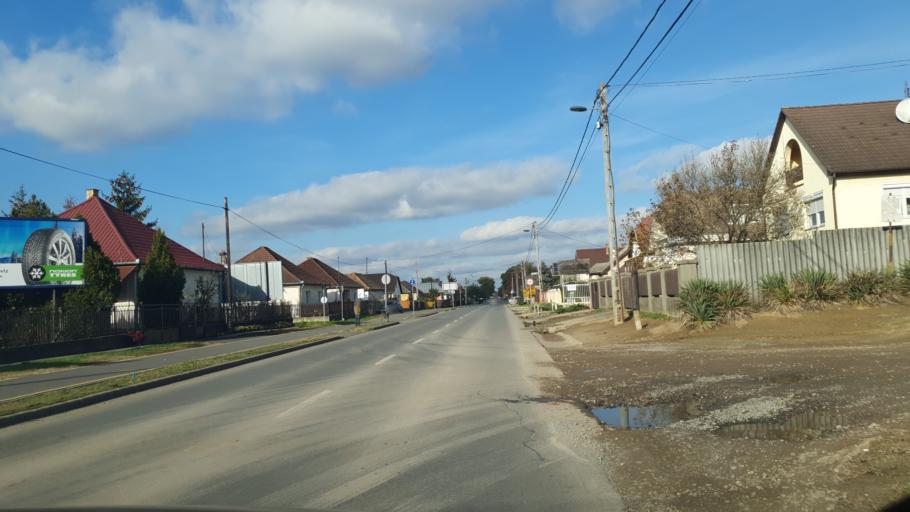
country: HU
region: Szabolcs-Szatmar-Bereg
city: Kisvarda
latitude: 48.2029
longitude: 22.0913
